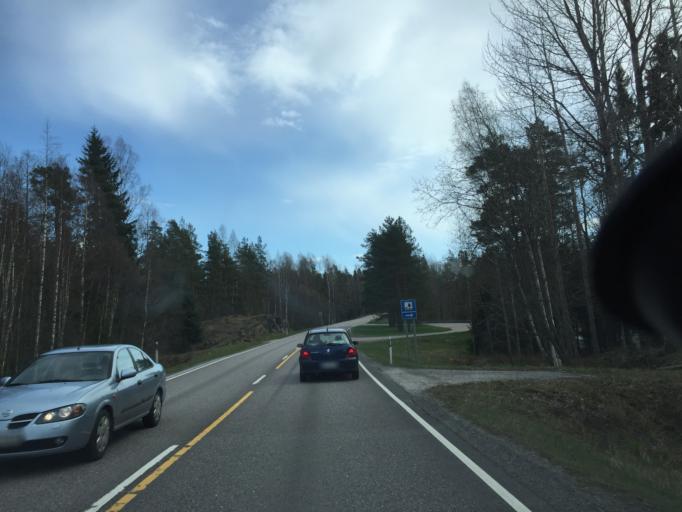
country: FI
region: Uusimaa
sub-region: Raaseporin
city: Ekenaes
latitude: 60.0239
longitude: 23.3746
